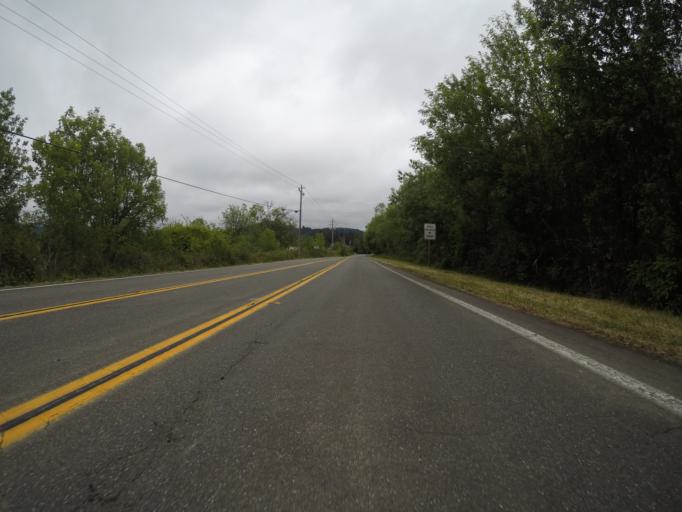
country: US
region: California
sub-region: Humboldt County
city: Rio Dell
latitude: 40.3982
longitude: -123.9462
